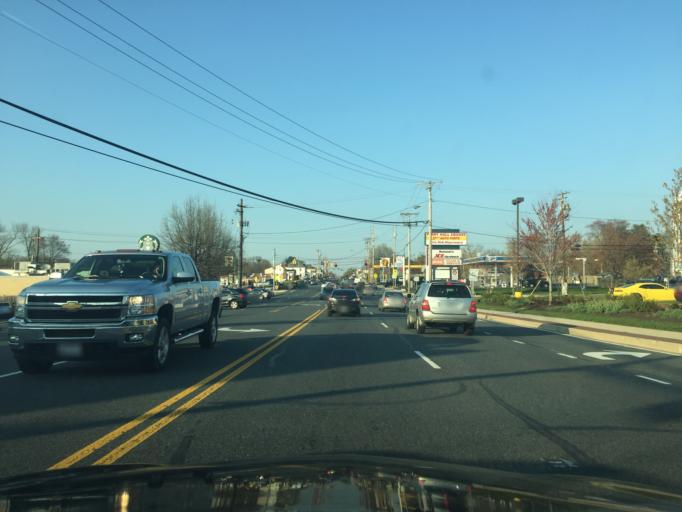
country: US
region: Maryland
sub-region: Baltimore County
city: Perry Hall
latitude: 39.3978
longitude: -76.4814
